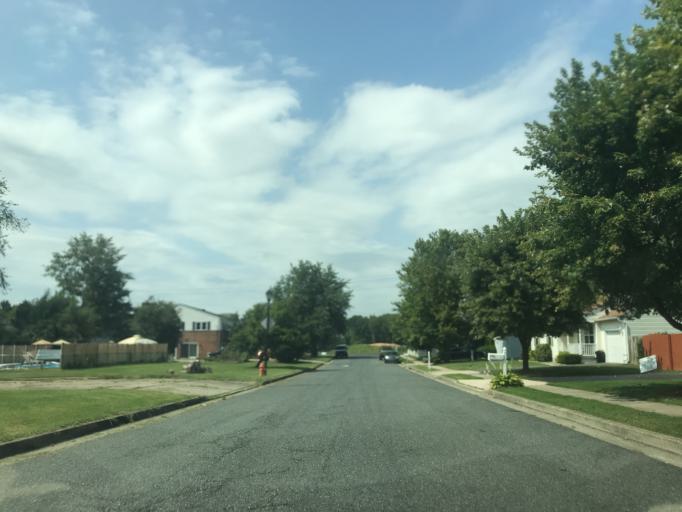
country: US
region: Maryland
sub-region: Baltimore County
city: Middle River
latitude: 39.3562
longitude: -76.4303
